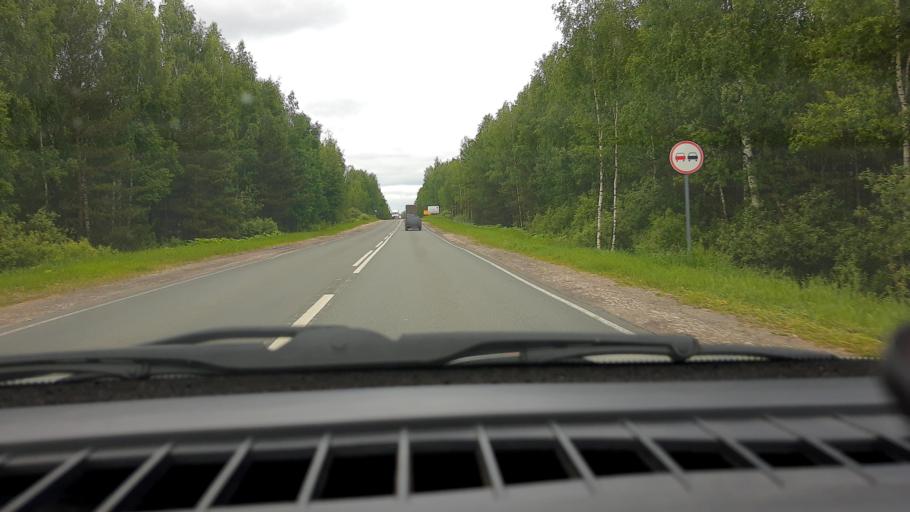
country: RU
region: Nizjnij Novgorod
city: Vladimirskoye
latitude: 56.8915
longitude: 44.9938
